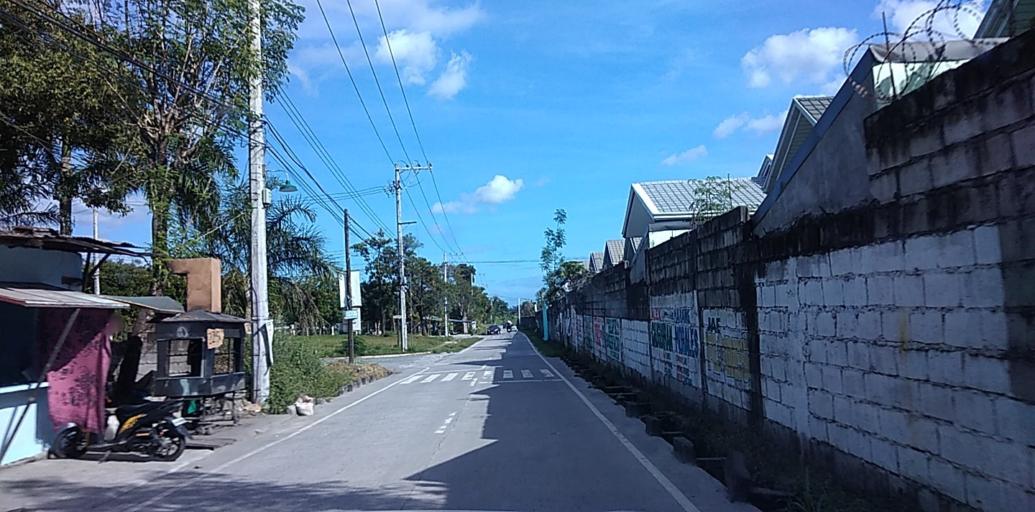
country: PH
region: Central Luzon
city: Santol
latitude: 15.1456
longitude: 120.5522
